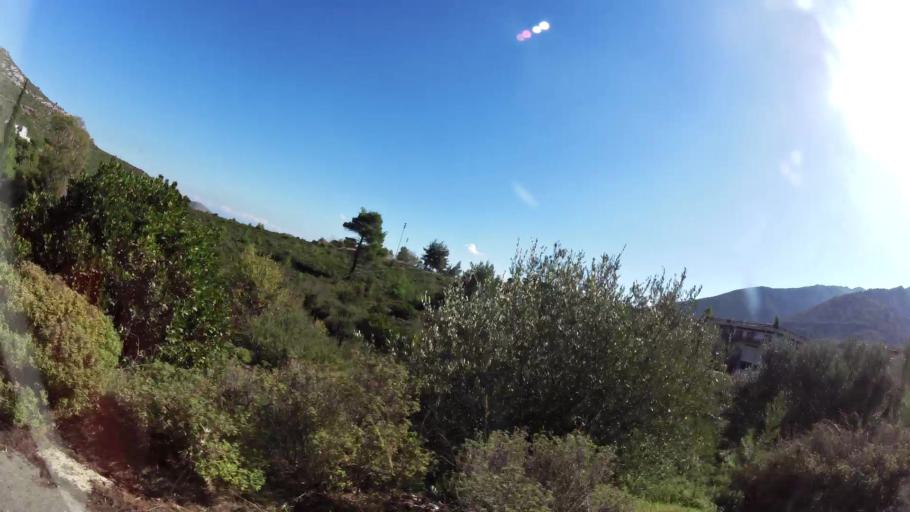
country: GR
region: Attica
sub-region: Nomarchia Anatolikis Attikis
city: Dionysos
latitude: 38.0978
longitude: 23.8900
